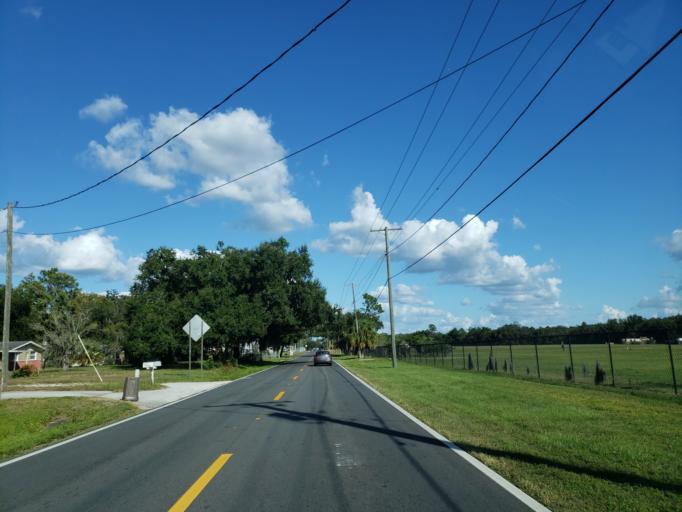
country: US
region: Florida
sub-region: Hillsborough County
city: Plant City
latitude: 28.0033
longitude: -82.1593
